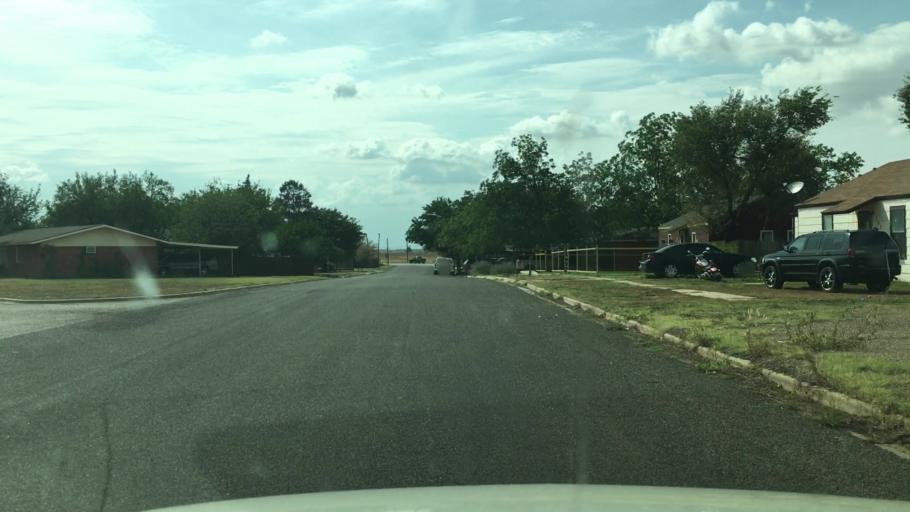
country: US
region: Texas
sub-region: Dawson County
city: Lamesa
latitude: 32.7526
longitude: -101.9546
